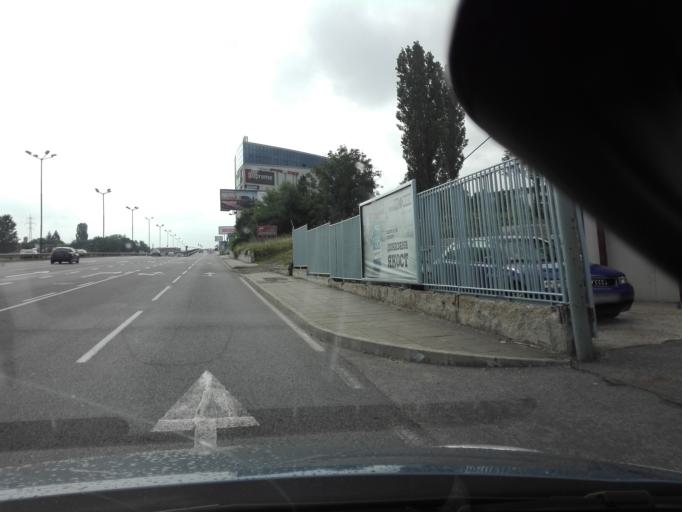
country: BG
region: Sofia-Capital
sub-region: Stolichna Obshtina
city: Sofia
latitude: 42.6436
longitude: 23.3071
